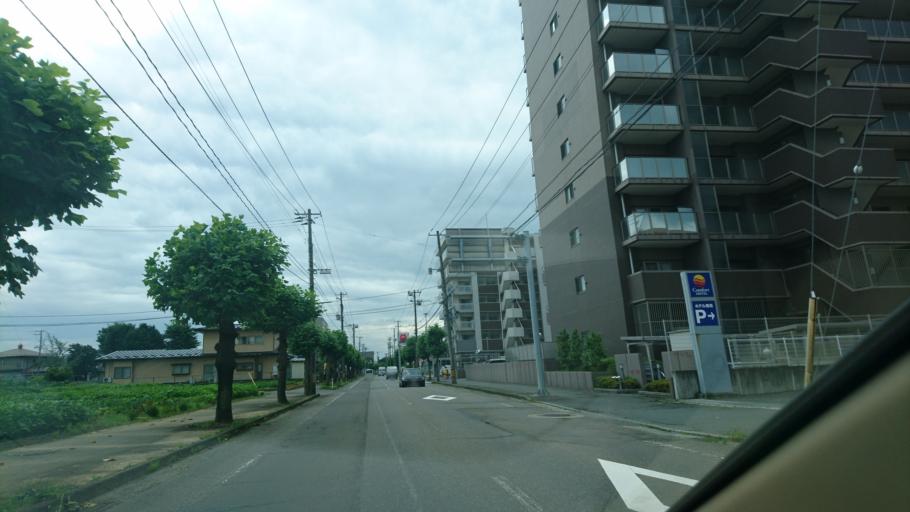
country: JP
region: Iwate
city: Kitakami
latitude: 39.2812
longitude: 141.1239
